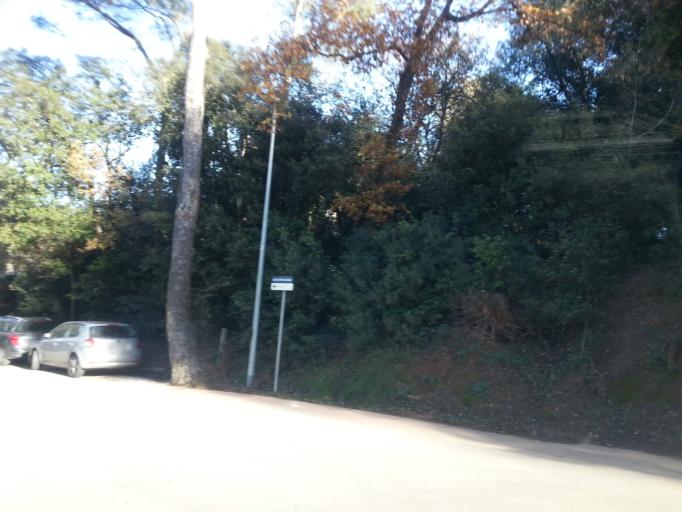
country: ES
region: Catalonia
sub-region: Provincia de Barcelona
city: Sant Cugat del Valles
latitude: 41.4263
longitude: 2.0898
